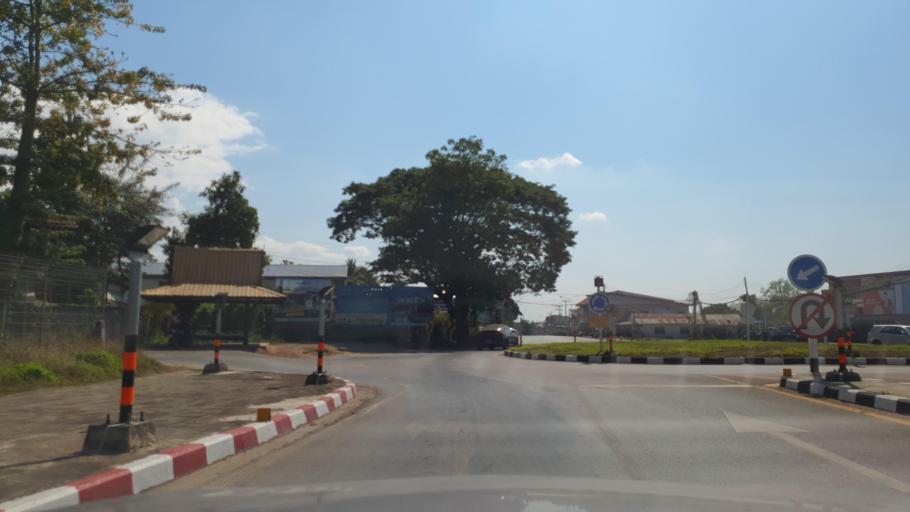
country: TH
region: Nan
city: Nan
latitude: 18.7964
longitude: 100.7793
